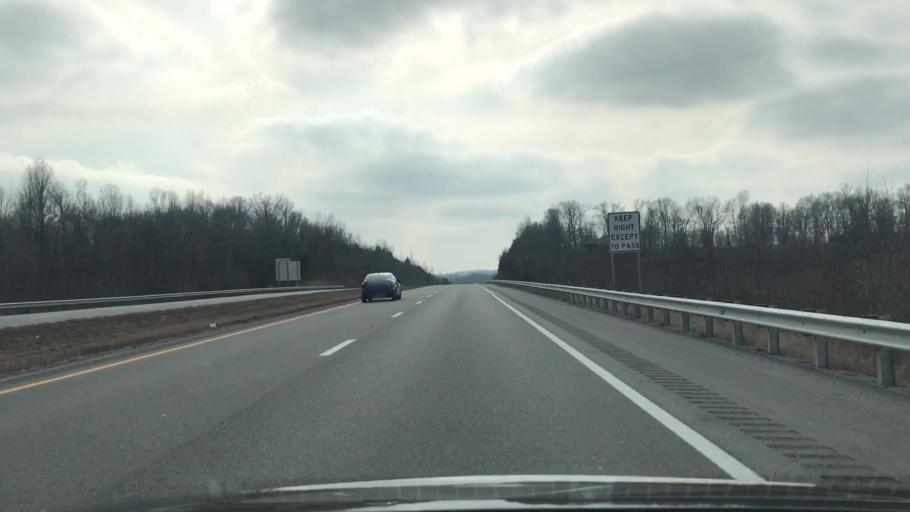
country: US
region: Kentucky
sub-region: Hopkins County
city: Nortonville
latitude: 37.1799
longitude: -87.4465
